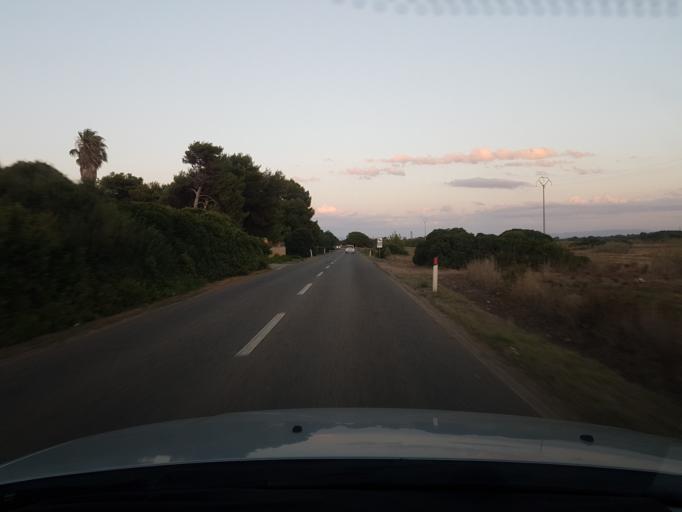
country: IT
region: Sardinia
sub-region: Provincia di Oristano
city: Riola Sardo
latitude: 40.0223
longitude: 8.4502
